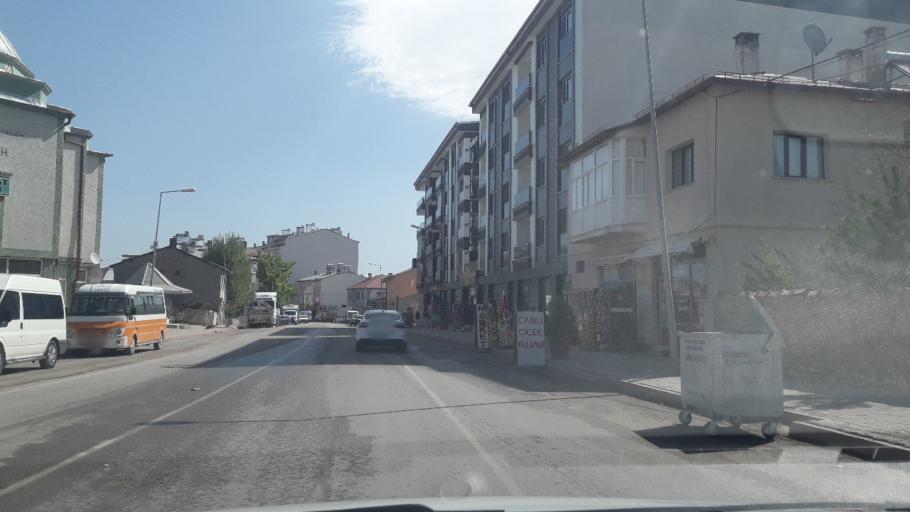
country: TR
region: Sivas
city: Kangal
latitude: 39.2322
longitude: 37.3891
